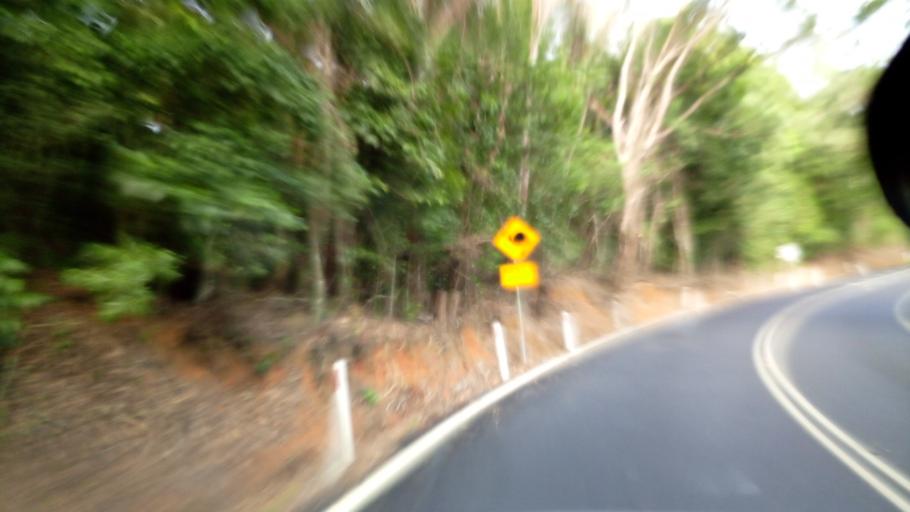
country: AU
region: Queensland
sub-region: Tablelands
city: Kuranda
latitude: -16.8325
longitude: 145.6685
